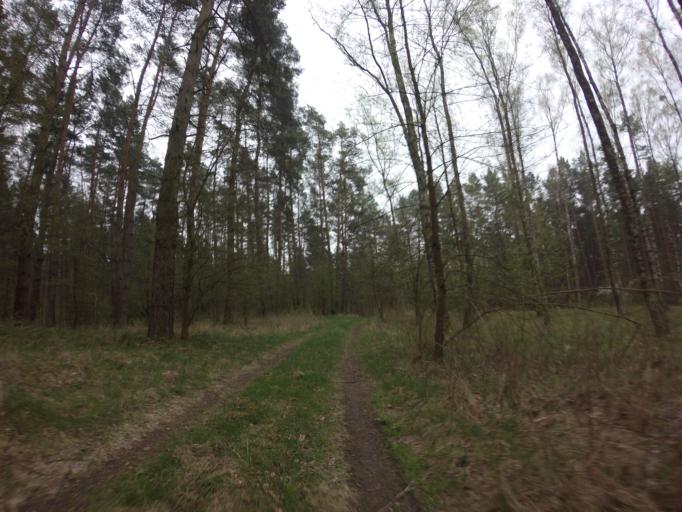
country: PL
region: West Pomeranian Voivodeship
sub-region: Powiat choszczenski
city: Recz
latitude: 53.1865
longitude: 15.5293
